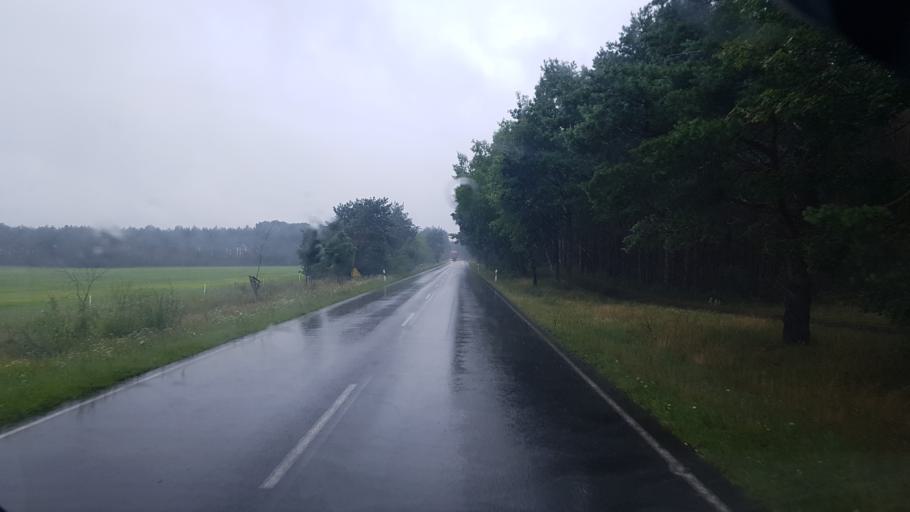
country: DE
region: Brandenburg
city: Golssen
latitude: 52.0507
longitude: 13.5883
